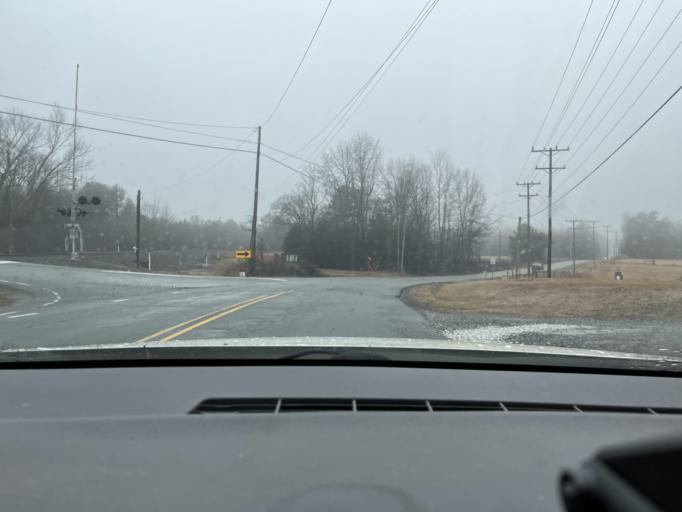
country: US
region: North Carolina
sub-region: Guilford County
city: Pleasant Garden
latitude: 35.9806
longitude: -79.7771
